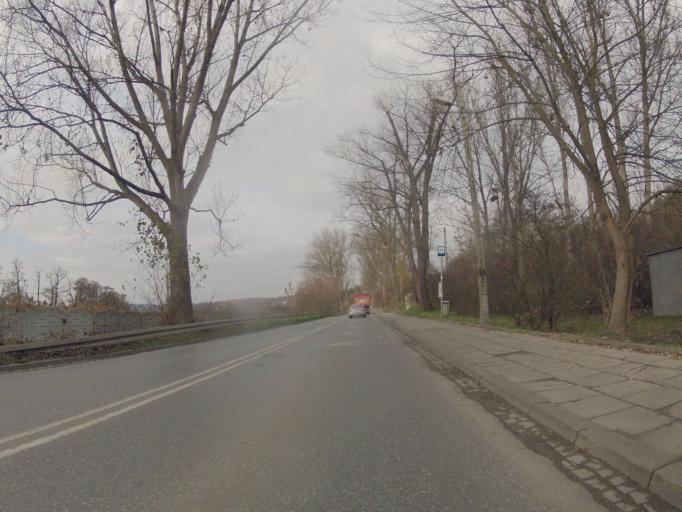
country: PL
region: Lesser Poland Voivodeship
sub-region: Powiat krakowski
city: Rzaska
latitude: 50.0876
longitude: 19.8407
